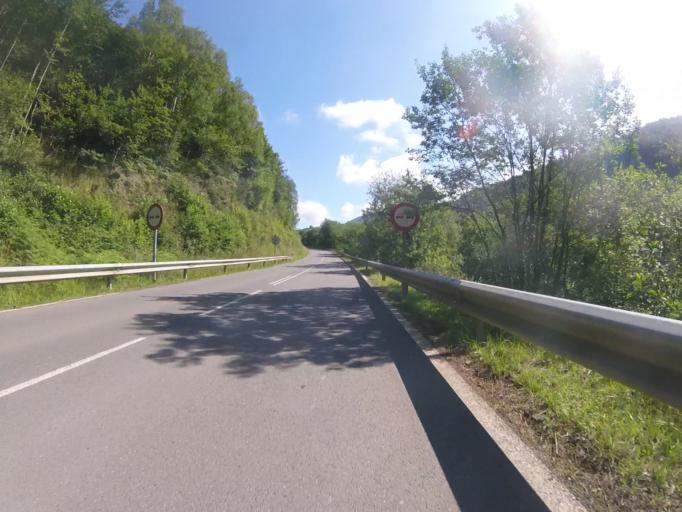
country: ES
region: Basque Country
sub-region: Provincia de Guipuzcoa
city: Beizama
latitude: 43.1179
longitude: -2.2280
